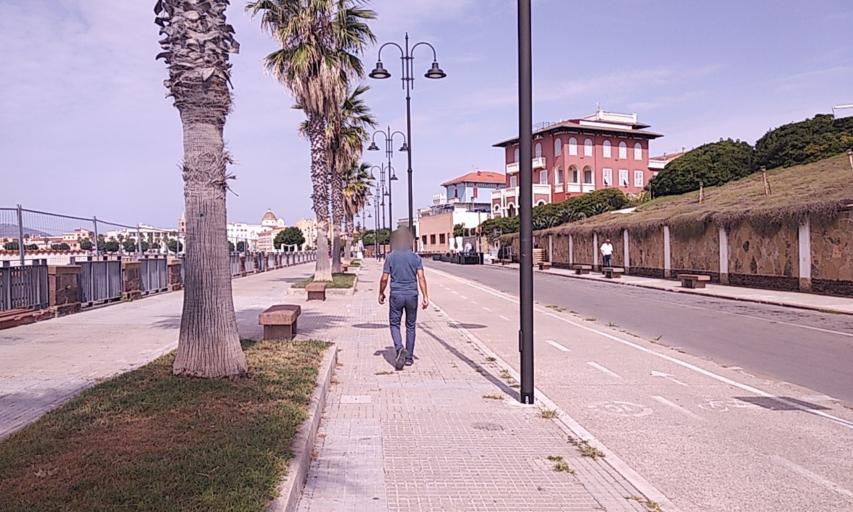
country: IT
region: Sardinia
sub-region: Provincia di Sassari
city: Alghero
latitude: 40.5530
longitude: 8.3162
